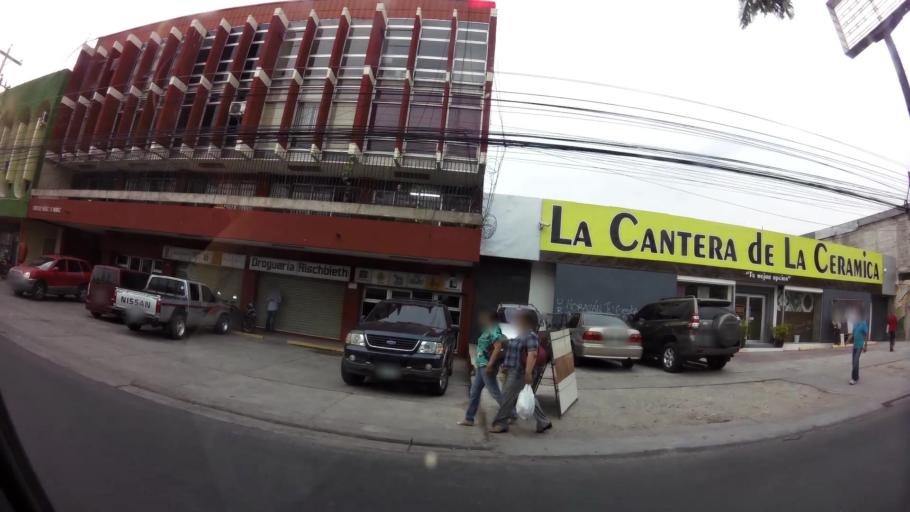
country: HN
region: Francisco Morazan
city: Tegucigalpa
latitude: 14.0998
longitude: -87.1961
